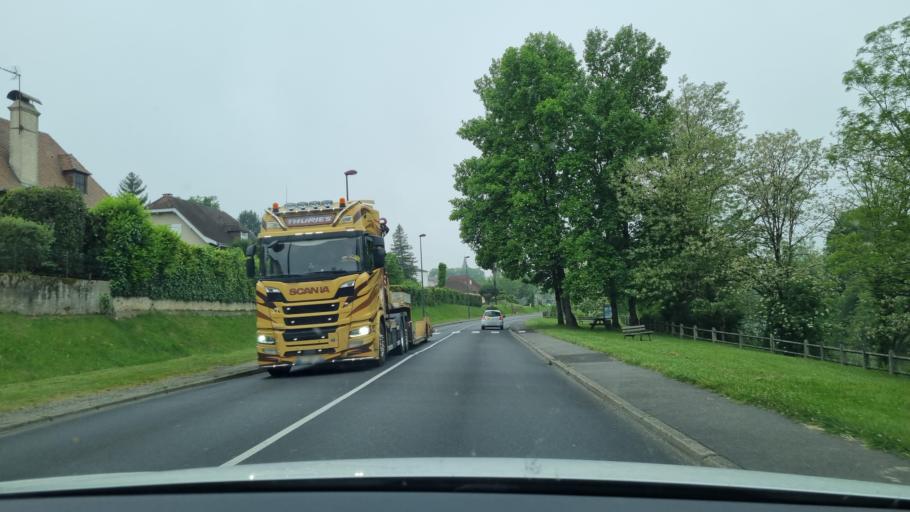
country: FR
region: Aquitaine
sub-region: Departement des Pyrenees-Atlantiques
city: Orthez
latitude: 43.4826
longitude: -0.7707
